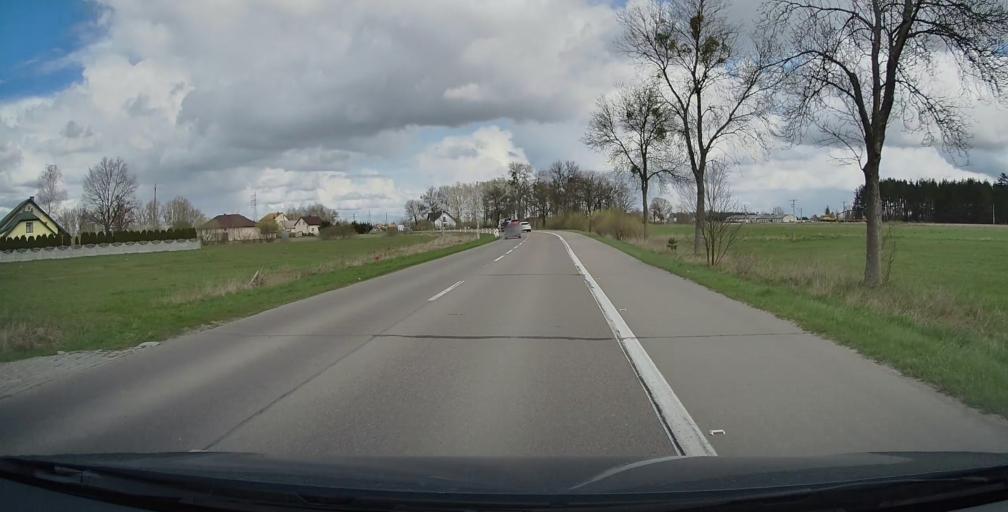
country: PL
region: Masovian Voivodeship
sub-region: Powiat ostrolecki
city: Rzekun
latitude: 53.0392
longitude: 21.5936
